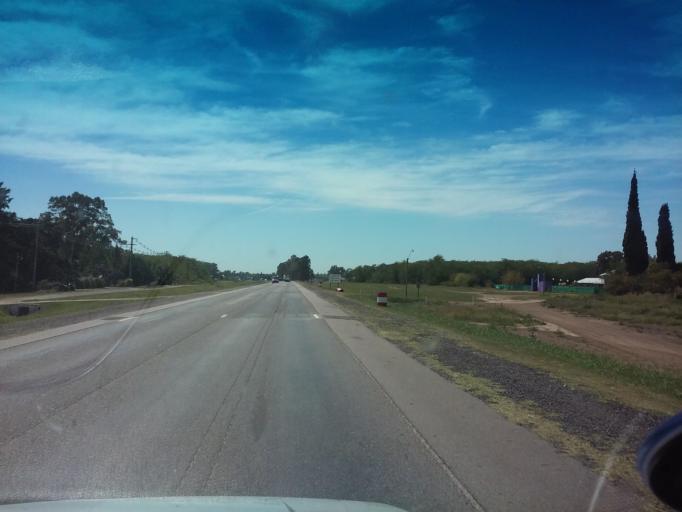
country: AR
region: Buenos Aires
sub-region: Partido de Mercedes
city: Mercedes
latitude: -34.6725
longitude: -59.4166
